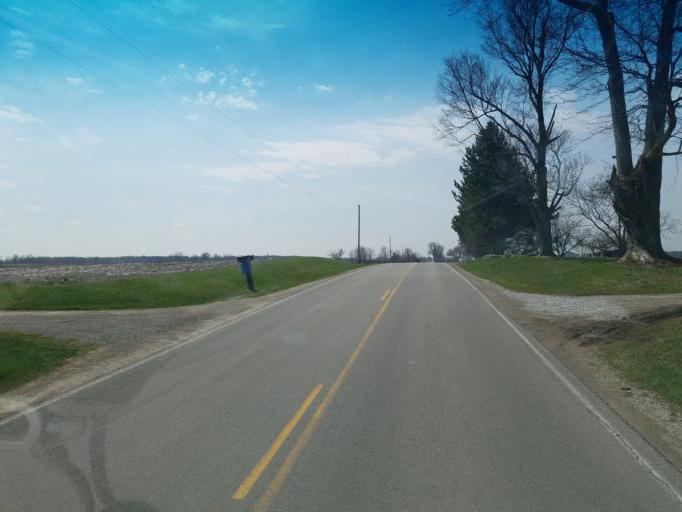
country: US
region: Ohio
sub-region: Crawford County
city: Bucyrus
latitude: 40.9204
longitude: -83.0933
